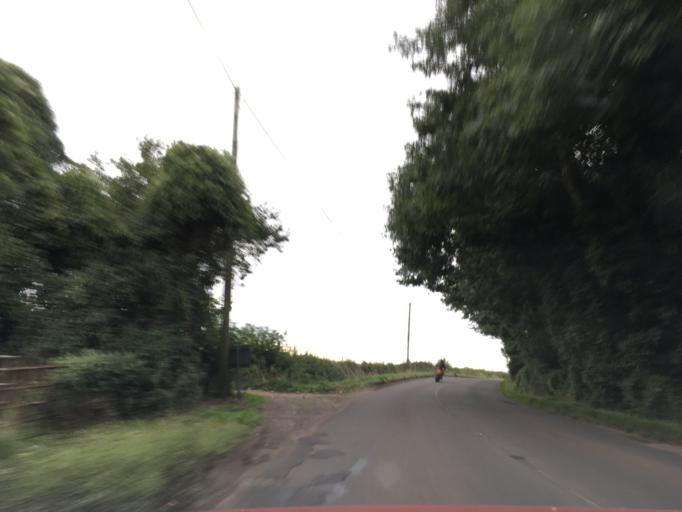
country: GB
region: England
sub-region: Wiltshire
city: Bremhill
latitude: 51.4229
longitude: -2.0625
